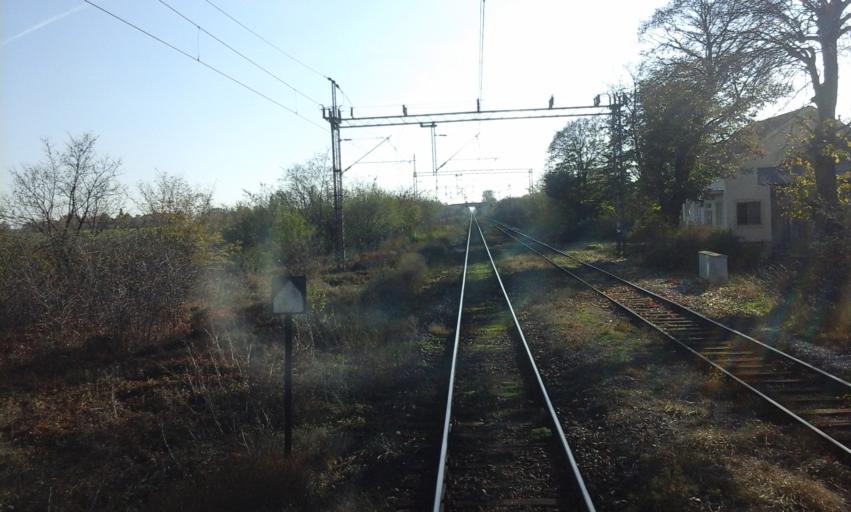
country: RS
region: Autonomna Pokrajina Vojvodina
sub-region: Severnobacki Okrug
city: Mali Igos
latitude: 45.7464
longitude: 19.6489
